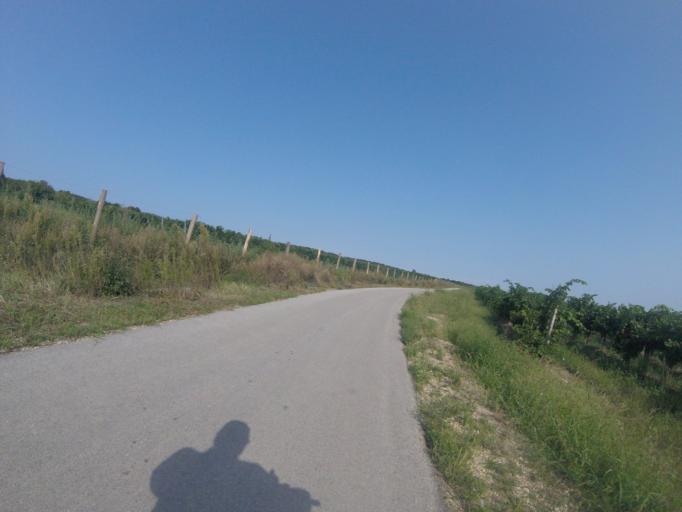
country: HU
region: Gyor-Moson-Sopron
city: Fertorakos
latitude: 47.6927
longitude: 16.6605
